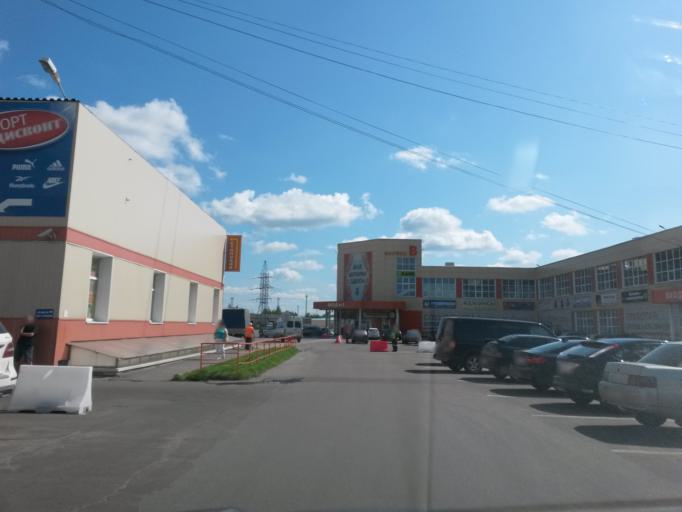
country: RU
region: Ivanovo
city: Bogorodskoye
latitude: 57.0106
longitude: 41.0079
